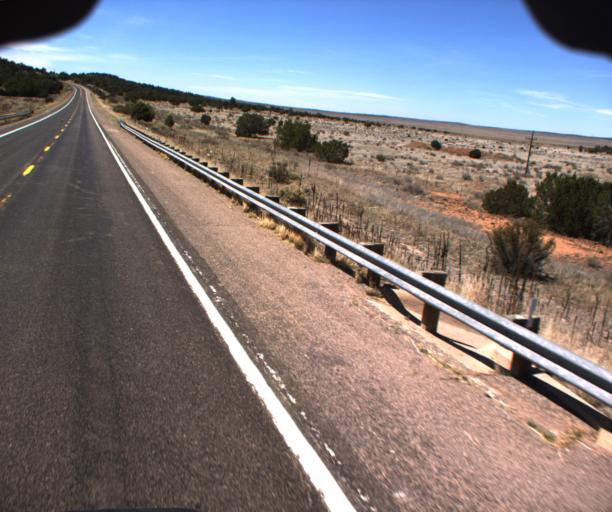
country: US
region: Arizona
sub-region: Mohave County
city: Peach Springs
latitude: 35.5220
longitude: -113.2085
